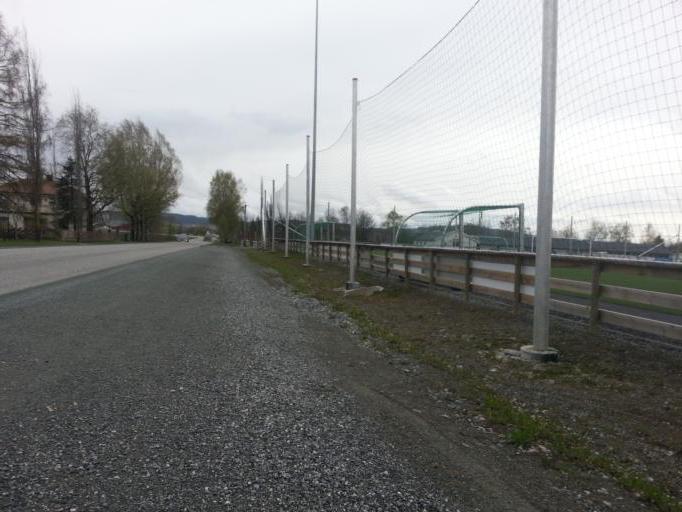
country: NO
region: Nord-Trondelag
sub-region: Levanger
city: Skogn
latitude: 63.7010
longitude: 11.1946
